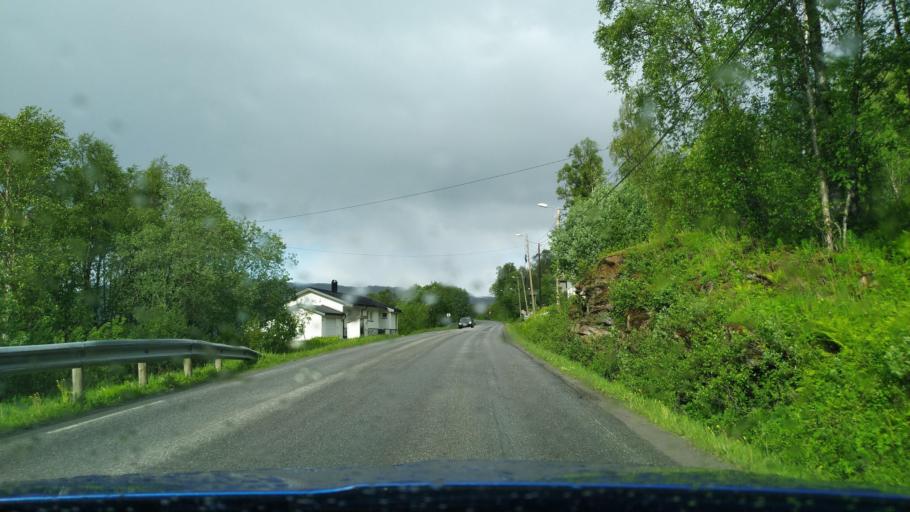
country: NO
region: Troms
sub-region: Sorreisa
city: Sorreisa
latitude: 69.1378
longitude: 18.0956
